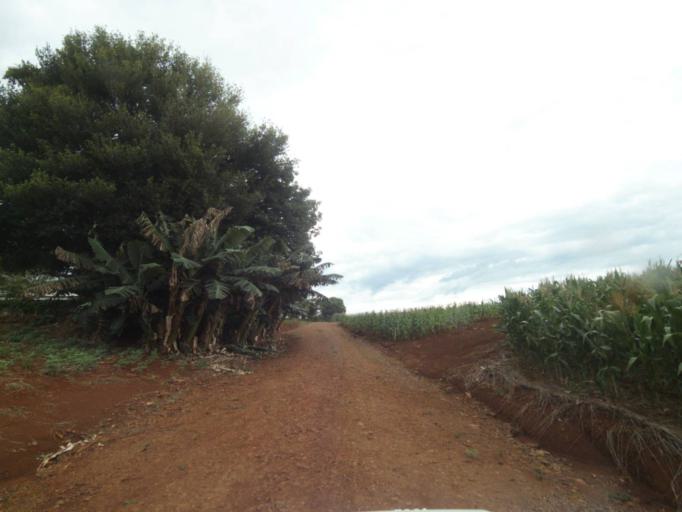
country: BR
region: Parana
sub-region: Guaraniacu
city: Guaraniacu
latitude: -24.9221
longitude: -52.9406
